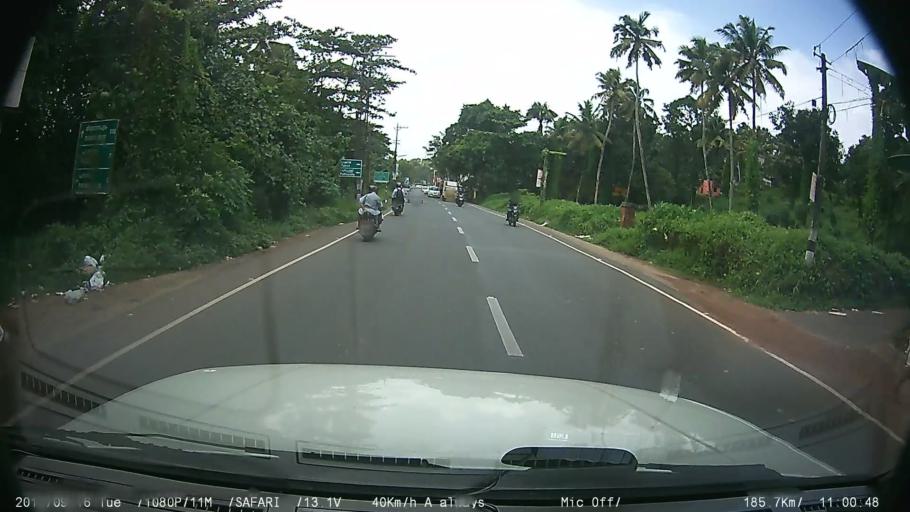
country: IN
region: Kerala
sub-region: Kottayam
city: Kottayam
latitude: 9.5612
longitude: 76.5156
